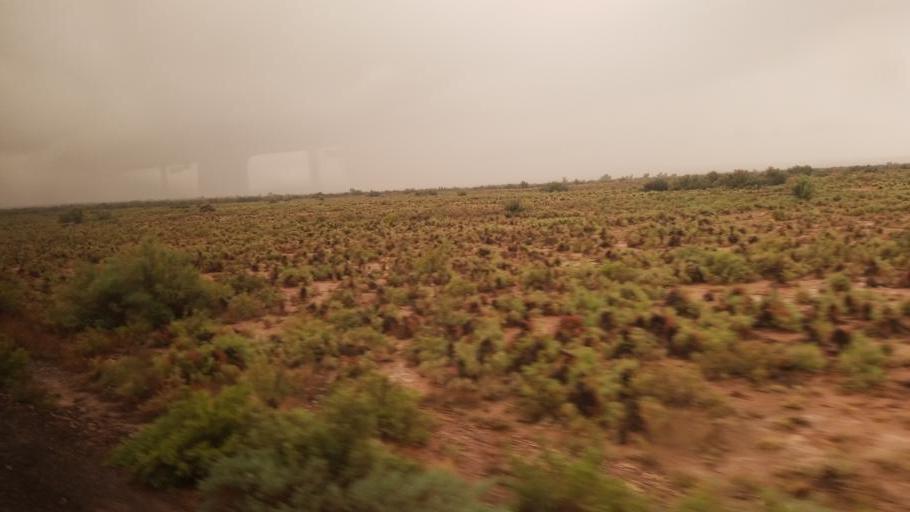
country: US
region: Arizona
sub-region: Navajo County
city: Joseph City
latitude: 34.9675
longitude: -110.4710
